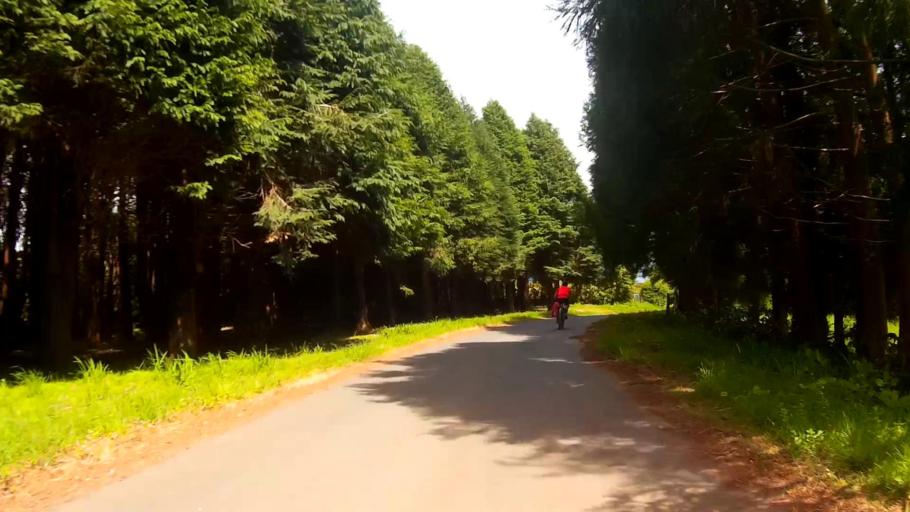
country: PT
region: Azores
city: Ribeira Grande
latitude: 38.5528
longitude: -28.6741
